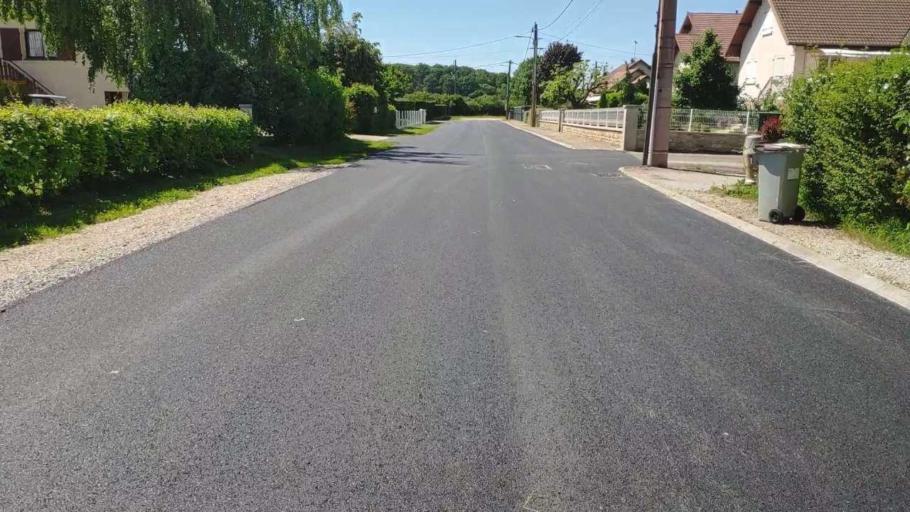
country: FR
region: Franche-Comte
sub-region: Departement du Jura
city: Perrigny
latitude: 46.7510
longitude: 5.6075
